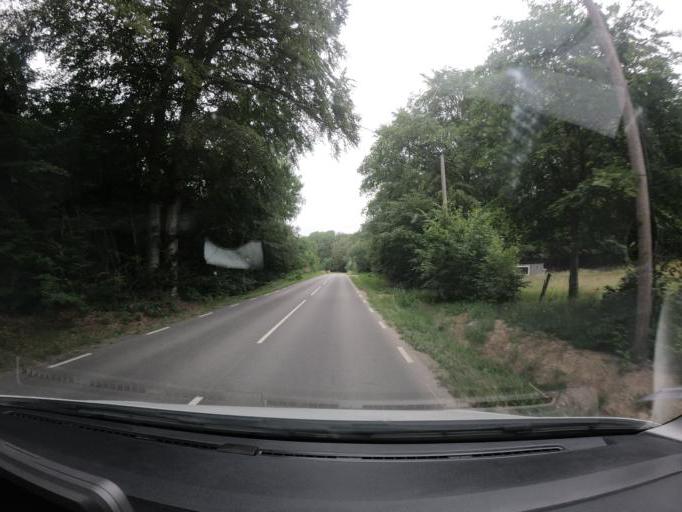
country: SE
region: Skane
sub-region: Perstorps Kommun
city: Perstorp
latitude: 56.0717
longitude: 13.3891
